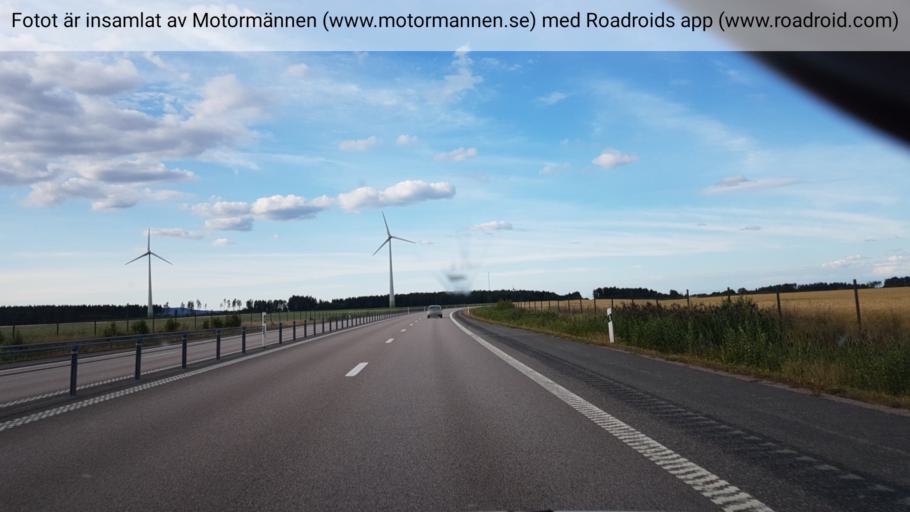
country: SE
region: Vaestra Goetaland
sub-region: Gotene Kommun
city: Goetene
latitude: 58.4748
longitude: 13.4778
